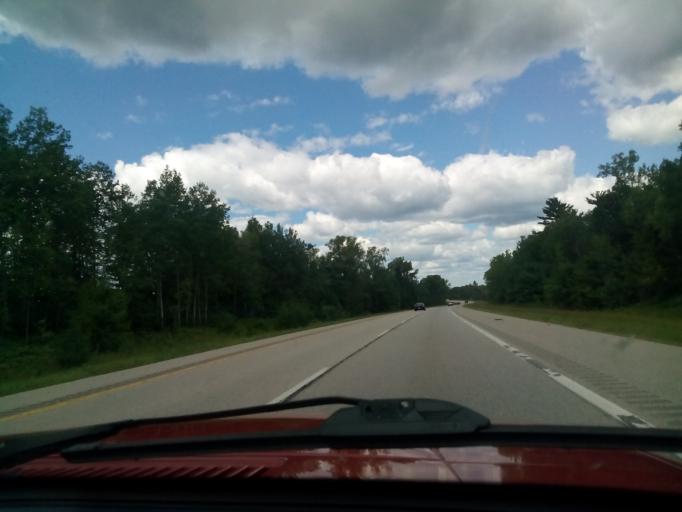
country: US
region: Michigan
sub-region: Ogemaw County
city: Skidway Lake
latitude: 44.0672
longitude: -84.0882
